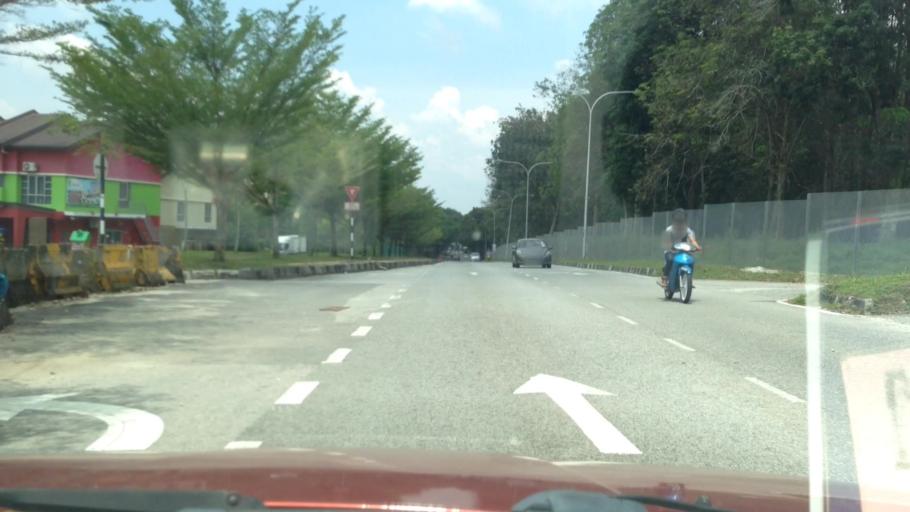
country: MY
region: Selangor
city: Kampung Baru Subang
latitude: 3.1673
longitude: 101.5514
